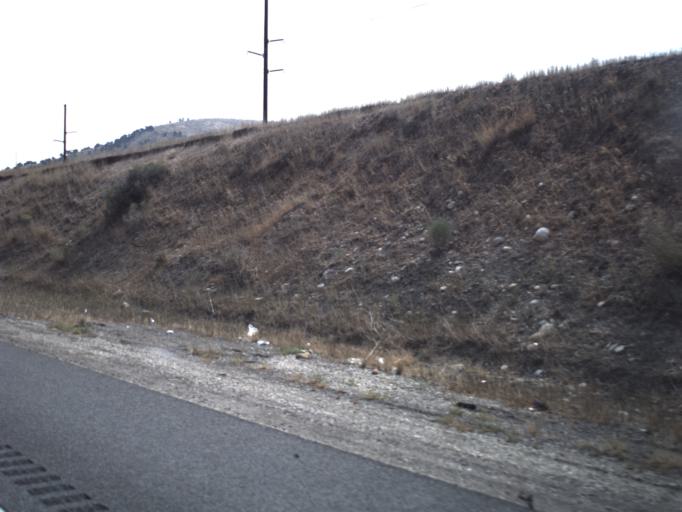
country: US
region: Utah
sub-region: Summit County
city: Coalville
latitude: 40.9479
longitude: -111.4193
